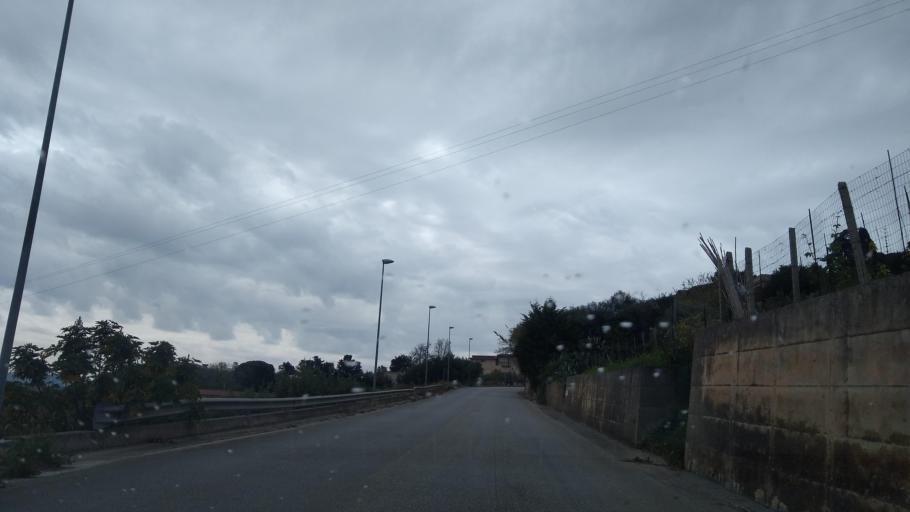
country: IT
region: Sicily
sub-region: Trapani
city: Alcamo
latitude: 38.0102
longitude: 12.9543
